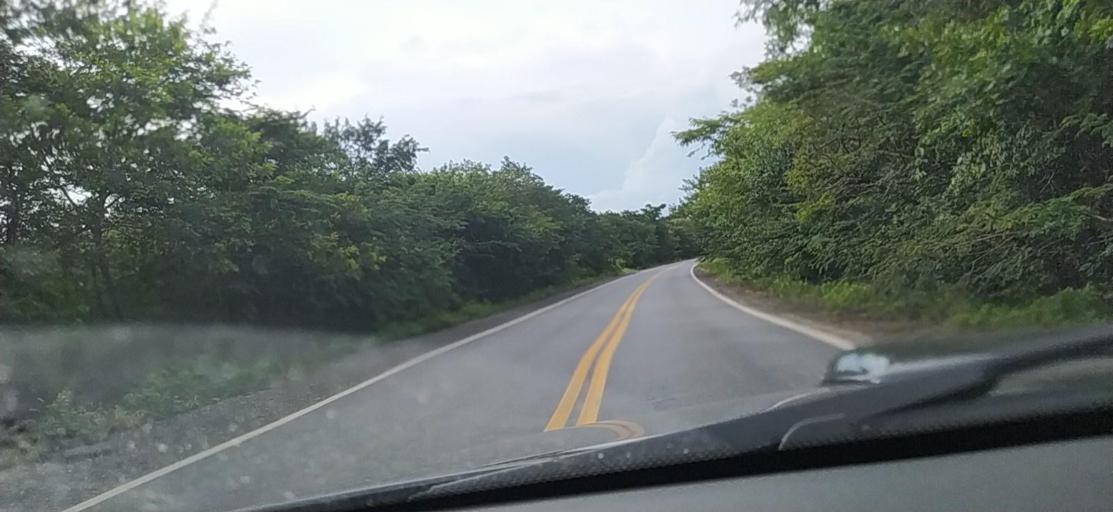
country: BR
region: Minas Gerais
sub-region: Francisco Sa
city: Francisco Sa
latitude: -16.5285
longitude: -43.6791
